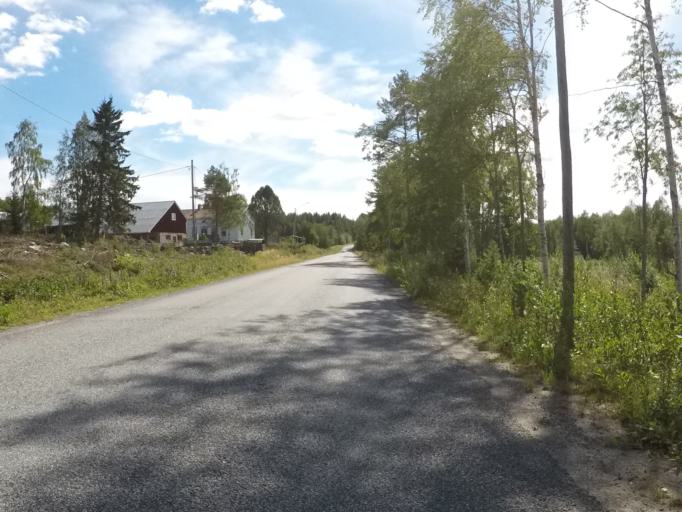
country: SE
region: Vaesterbotten
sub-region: Robertsfors Kommun
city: Robertsfors
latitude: 63.9945
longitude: 20.8082
